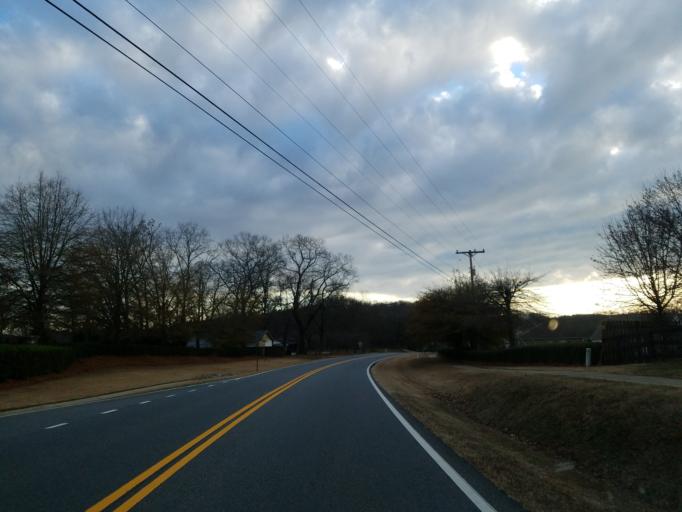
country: US
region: Georgia
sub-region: Forsyth County
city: Cumming
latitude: 34.2989
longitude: -84.0821
